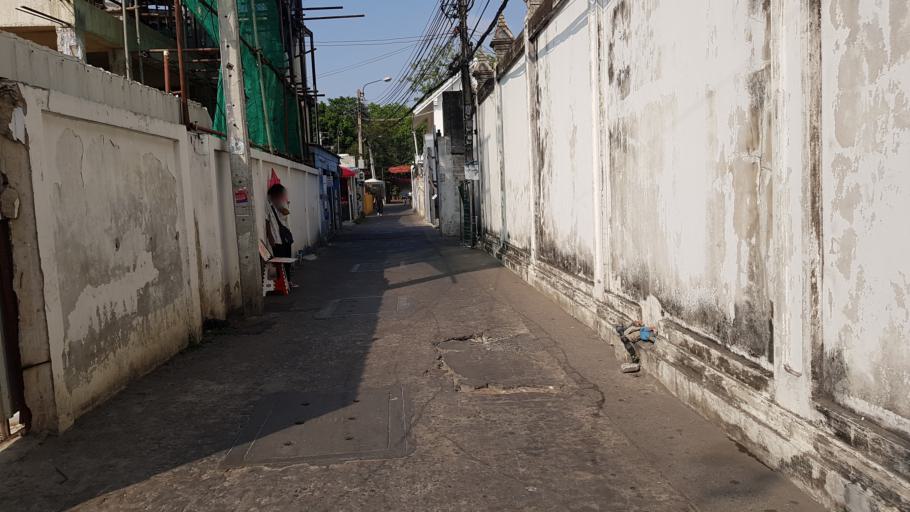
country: TH
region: Bangkok
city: Bangkok Noi
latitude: 13.7530
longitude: 100.4862
